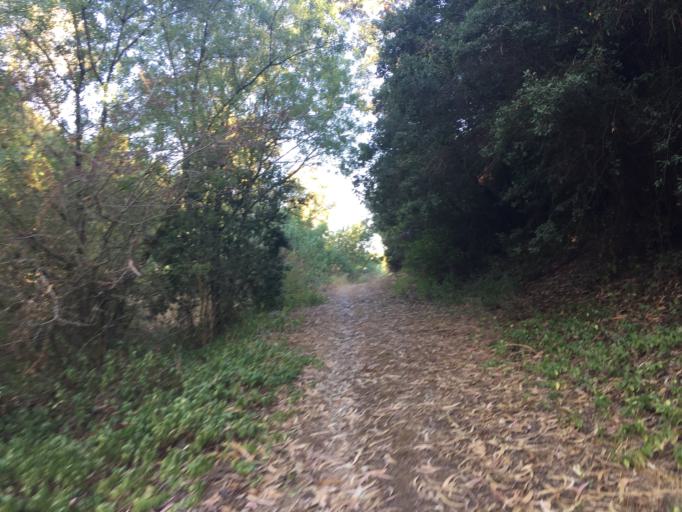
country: PT
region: Lisbon
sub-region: Alenquer
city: Alenquer
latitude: 39.1138
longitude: -8.9960
